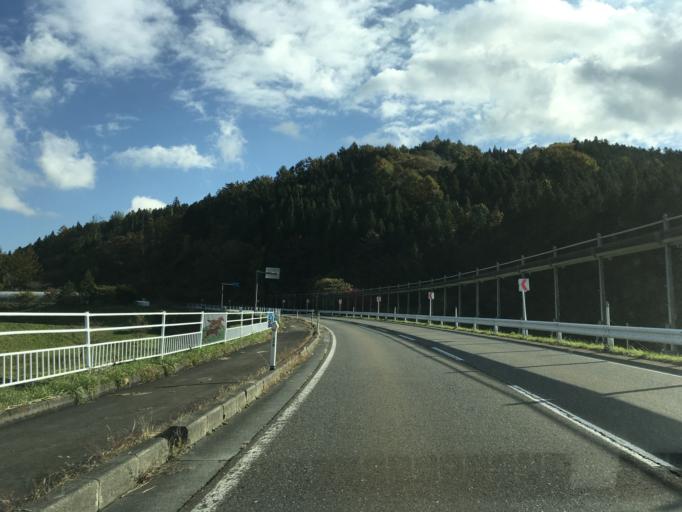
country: JP
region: Iwate
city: Tono
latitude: 39.3638
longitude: 141.4012
